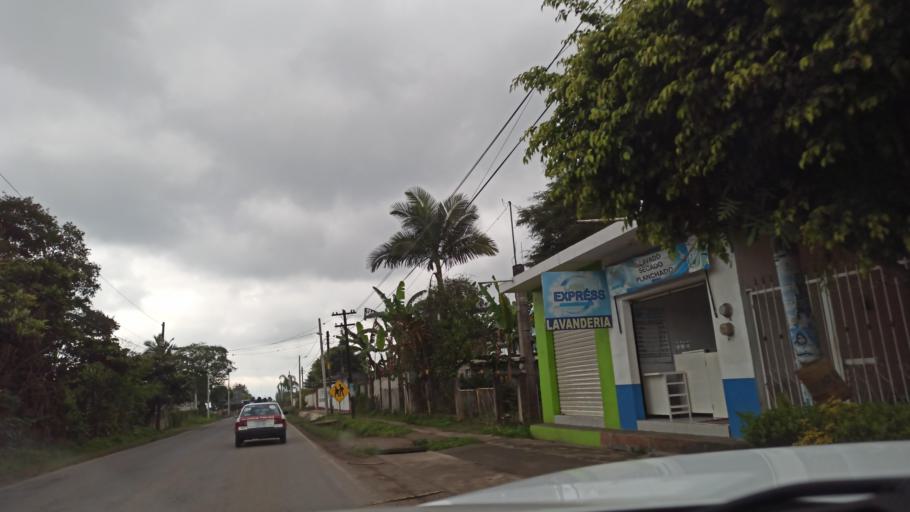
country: MX
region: Veracruz
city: Monte Blanco
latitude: 18.9589
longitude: -97.0181
